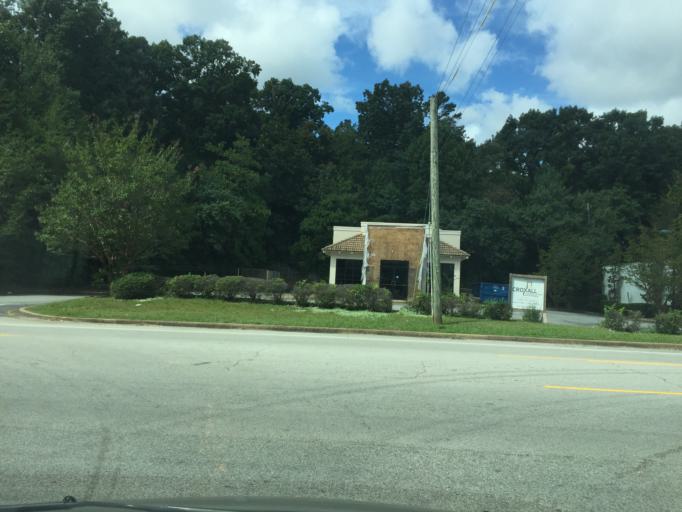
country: US
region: Tennessee
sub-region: Hamilton County
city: Signal Mountain
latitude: 35.1388
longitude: -85.3295
